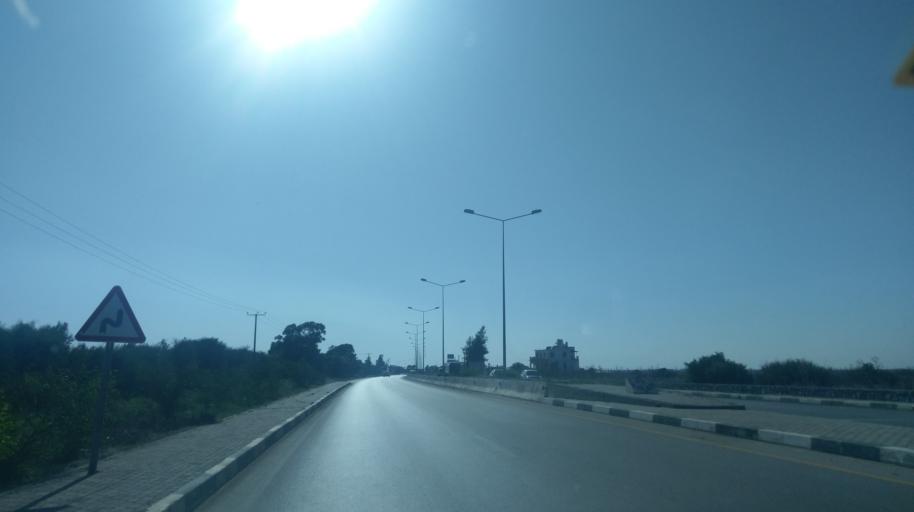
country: CY
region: Ammochostos
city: Trikomo
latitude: 35.2295
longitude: 33.8977
